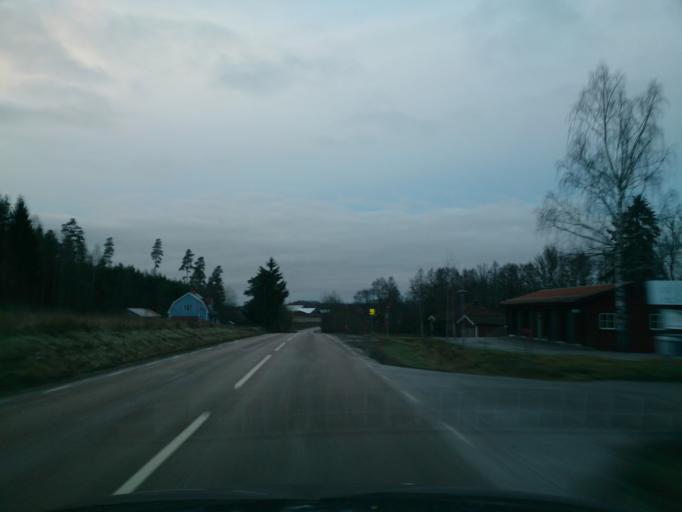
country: SE
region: OEstergoetland
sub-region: Linkopings Kommun
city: Linghem
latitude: 58.4395
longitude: 15.8911
